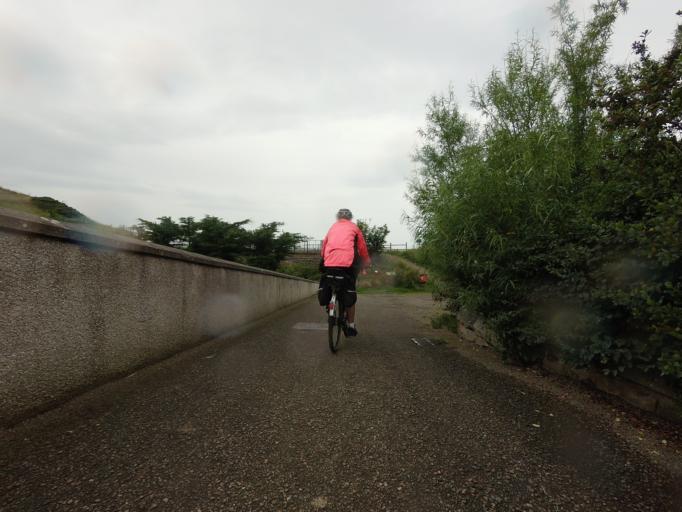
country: GB
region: Scotland
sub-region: Moray
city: Cullen
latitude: 57.6908
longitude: -2.8233
